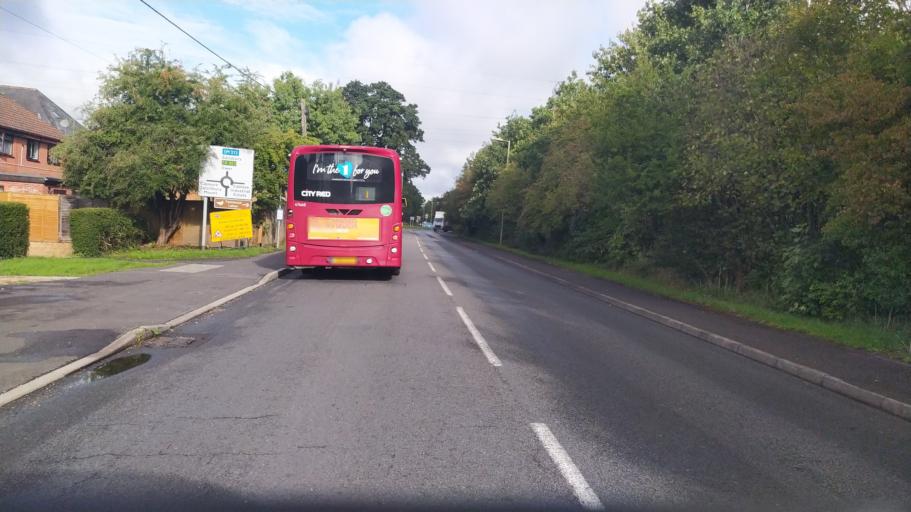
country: GB
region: England
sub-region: Hampshire
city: Totton
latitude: 50.9321
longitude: -1.5070
